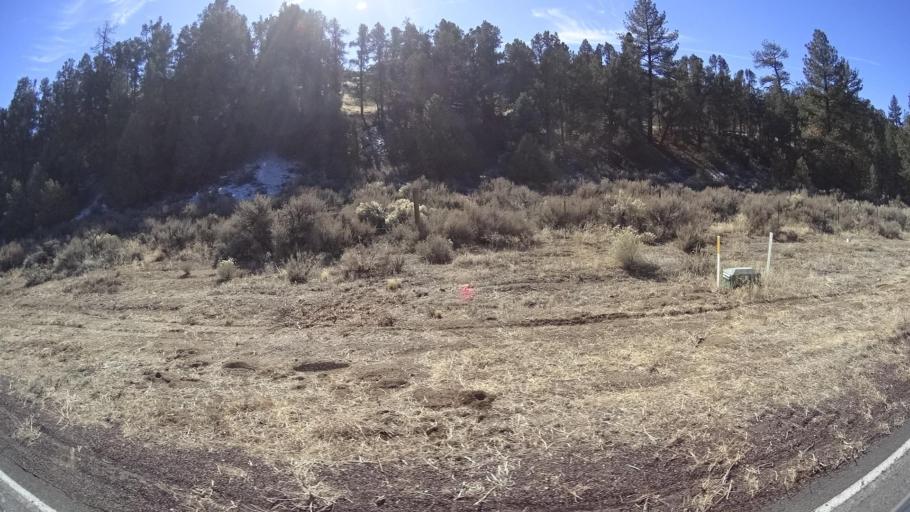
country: US
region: California
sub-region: Kern County
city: Frazier Park
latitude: 34.8264
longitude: -119.0170
